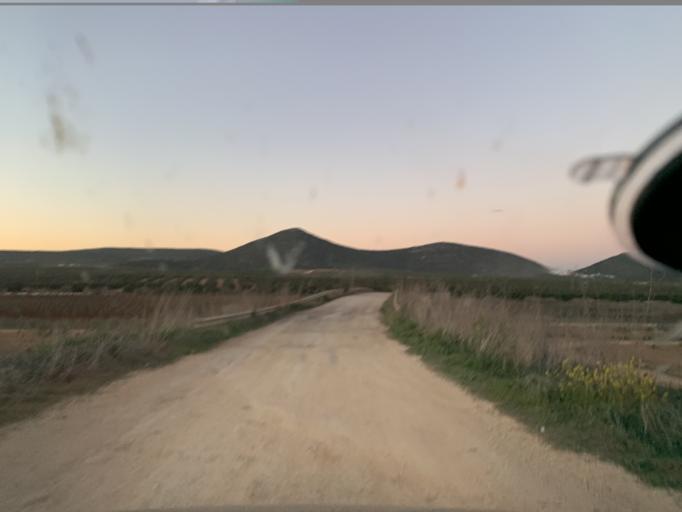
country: ES
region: Andalusia
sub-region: Provincia de Sevilla
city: Pedrera
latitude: 37.2121
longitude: -4.8515
